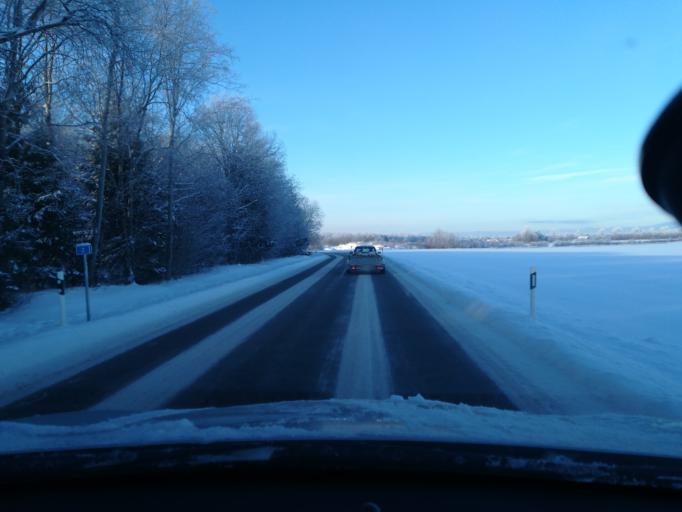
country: EE
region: Harju
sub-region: Saue linn
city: Saue
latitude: 59.3629
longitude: 24.5507
